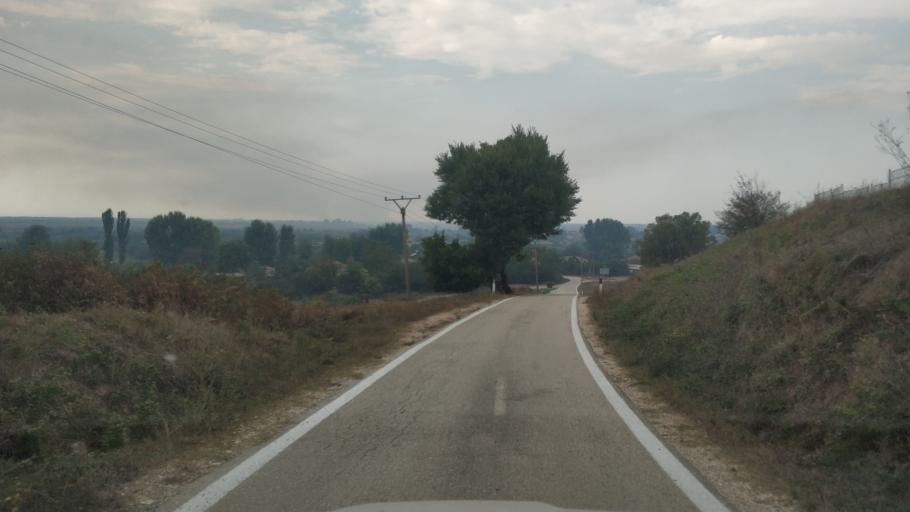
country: AL
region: Fier
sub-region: Rrethi i Fierit
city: Dermenas
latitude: 40.7243
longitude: 19.4690
